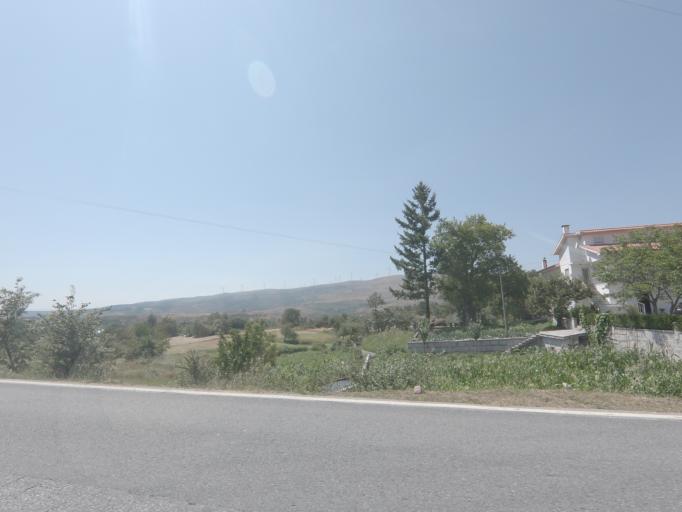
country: PT
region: Viseu
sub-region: Castro Daire
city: Castro Daire
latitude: 40.9627
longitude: -7.8853
